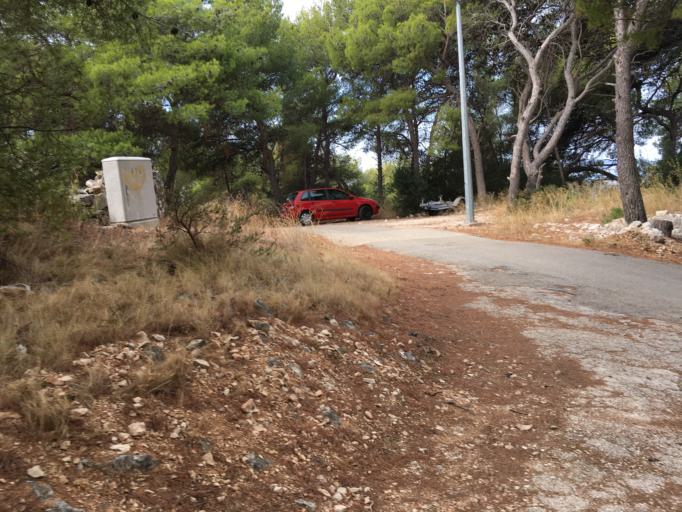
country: HR
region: Splitsko-Dalmatinska
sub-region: Grad Hvar
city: Hvar
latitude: 43.1650
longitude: 16.4434
